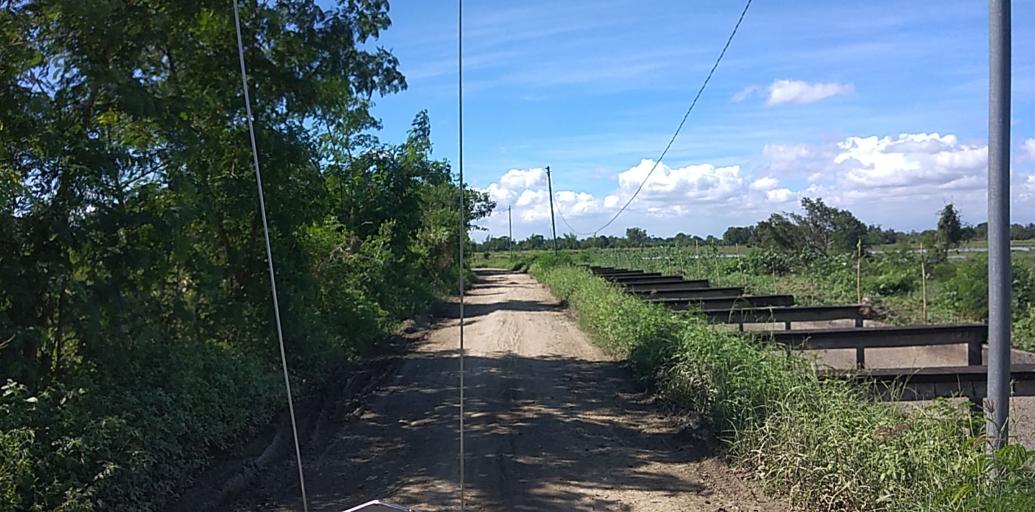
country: PH
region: Central Luzon
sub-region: Province of Pampanga
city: Candating
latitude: 15.1294
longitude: 120.8029
